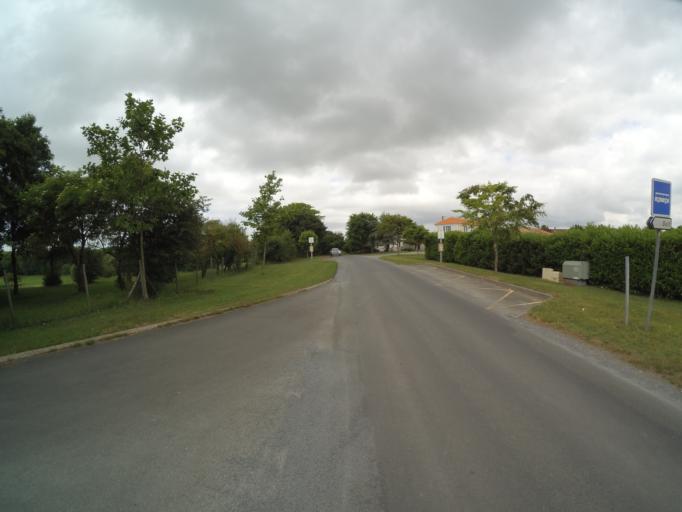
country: FR
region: Poitou-Charentes
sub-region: Departement de la Charente-Maritime
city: Saint-Laurent-de-la-Pree
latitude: 45.9851
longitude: -1.0087
